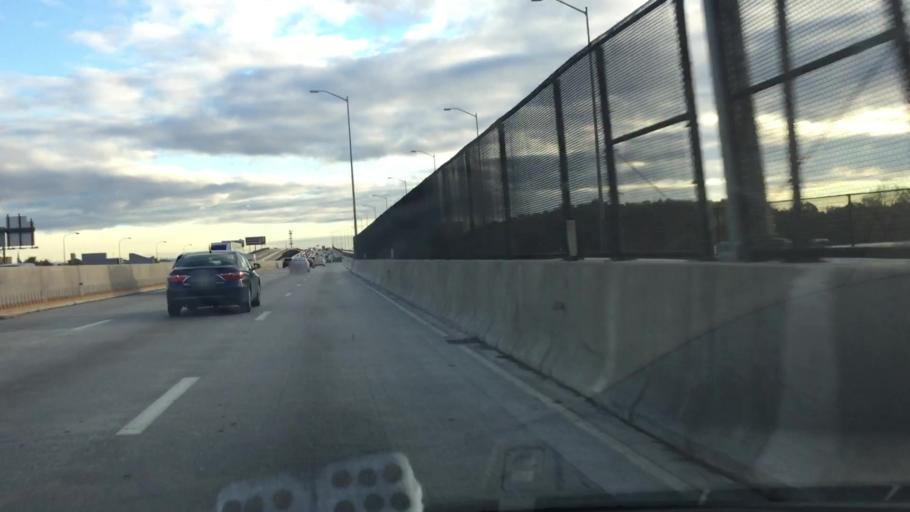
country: US
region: New Jersey
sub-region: Camden County
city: Camden
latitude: 39.9738
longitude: -75.1199
